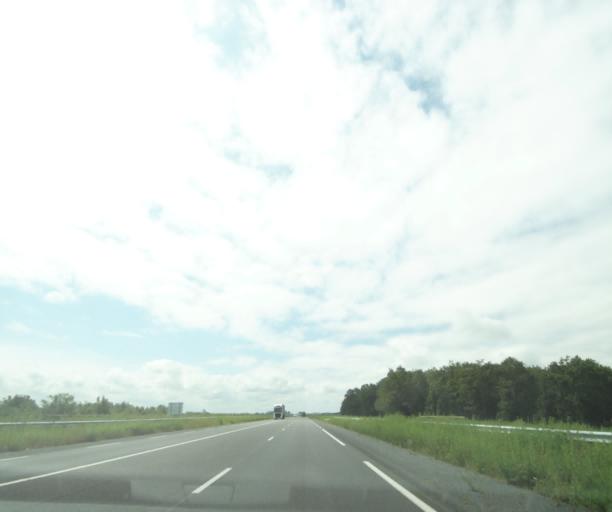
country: FR
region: Poitou-Charentes
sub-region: Departement des Deux-Sevres
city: Louzy
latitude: 47.0356
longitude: -0.1989
